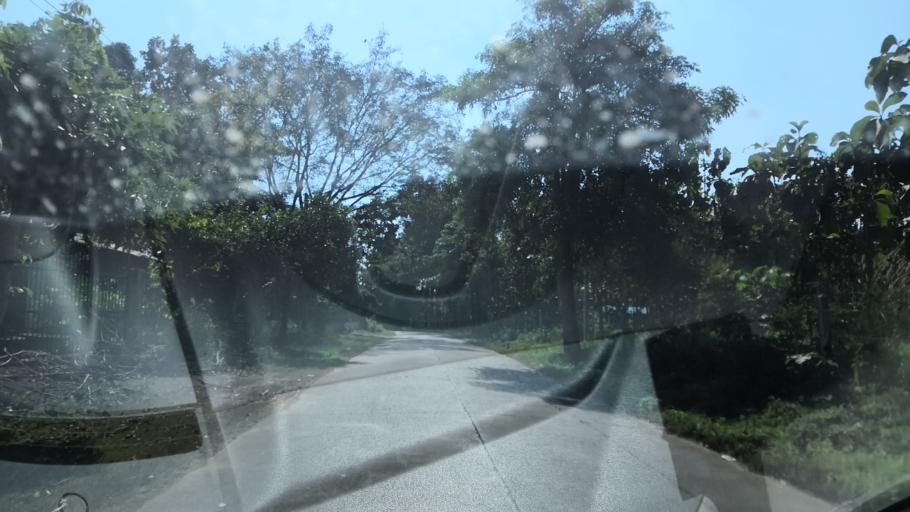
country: TH
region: Chiang Rai
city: Wiang Chai
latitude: 19.8816
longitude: 99.9418
